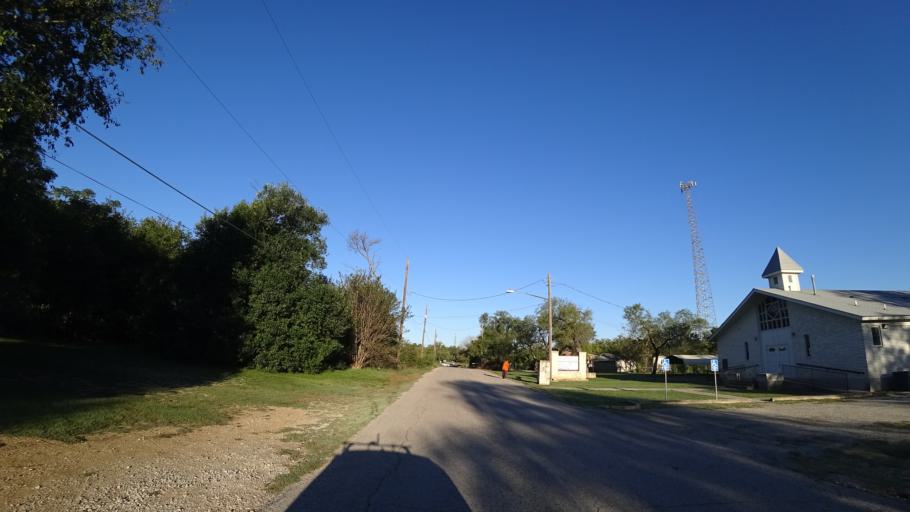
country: US
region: Texas
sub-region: Travis County
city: Hornsby Bend
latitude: 30.2035
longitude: -97.6375
